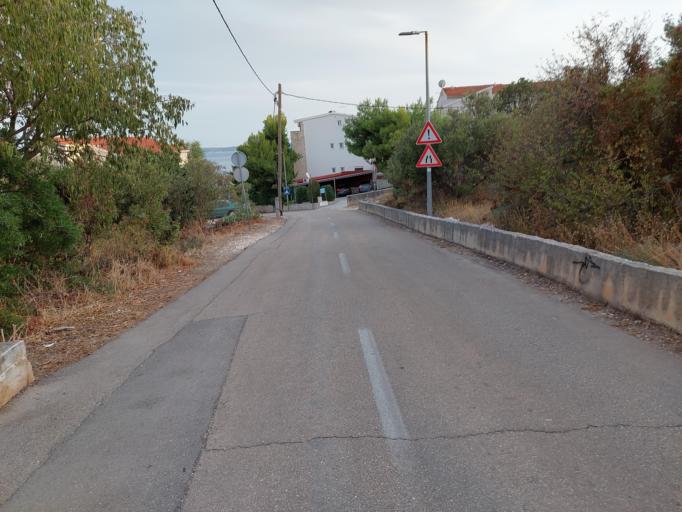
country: HR
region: Splitsko-Dalmatinska
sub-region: Grad Trogir
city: Trogir
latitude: 43.4940
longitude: 16.2706
